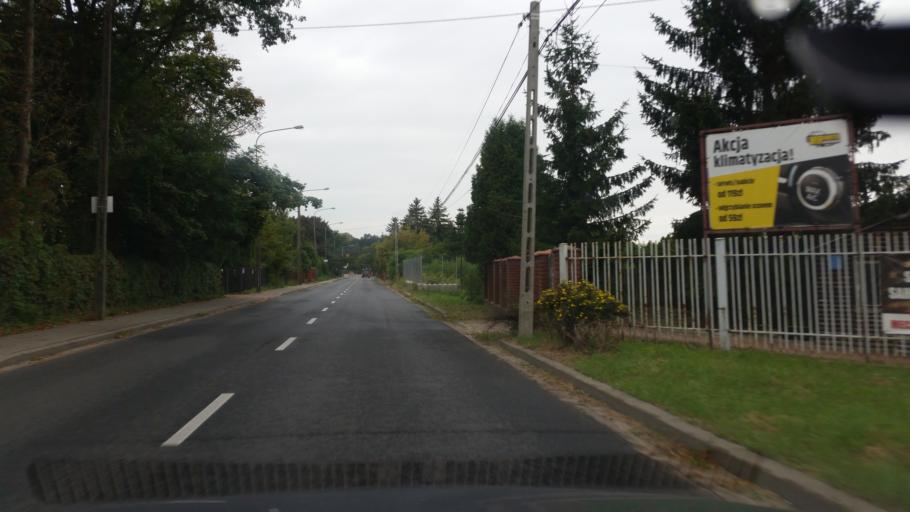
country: PL
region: Masovian Voivodeship
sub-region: Powiat piaseczynski
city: Konstancin-Jeziorna
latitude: 52.1053
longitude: 21.1105
